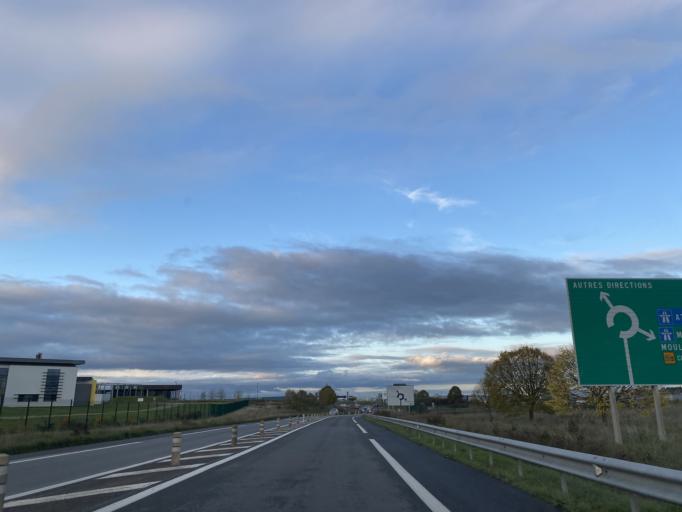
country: FR
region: Centre
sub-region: Departement du Cher
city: La Chapelle-Saint-Ursin
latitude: 47.0484
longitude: 2.3391
